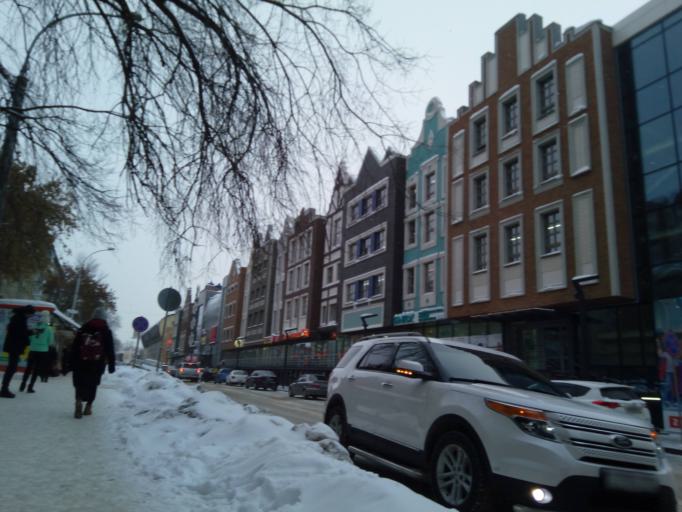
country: RU
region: Novosibirsk
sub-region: Novosibirskiy Rayon
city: Novosibirsk
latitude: 54.9904
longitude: 82.9027
